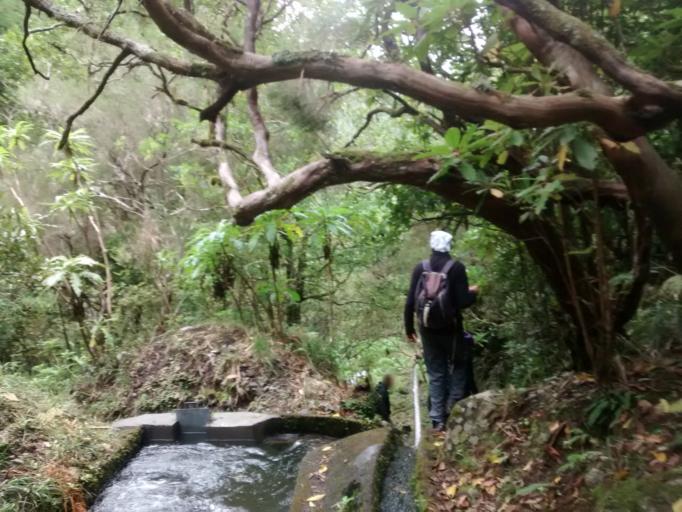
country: PT
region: Madeira
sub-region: Sao Vicente
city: Sao Vicente
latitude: 32.7572
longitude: -17.0476
